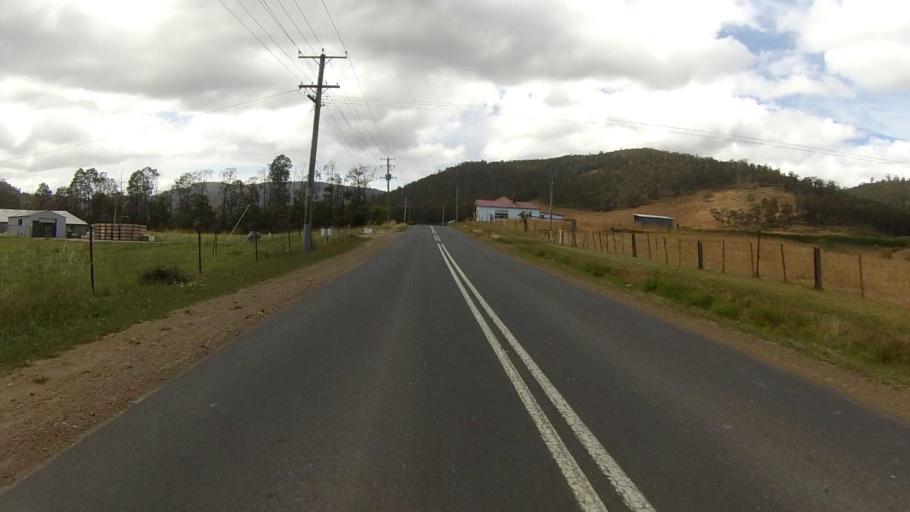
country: AU
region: Tasmania
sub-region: Huon Valley
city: Cygnet
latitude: -43.1651
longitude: 147.1296
